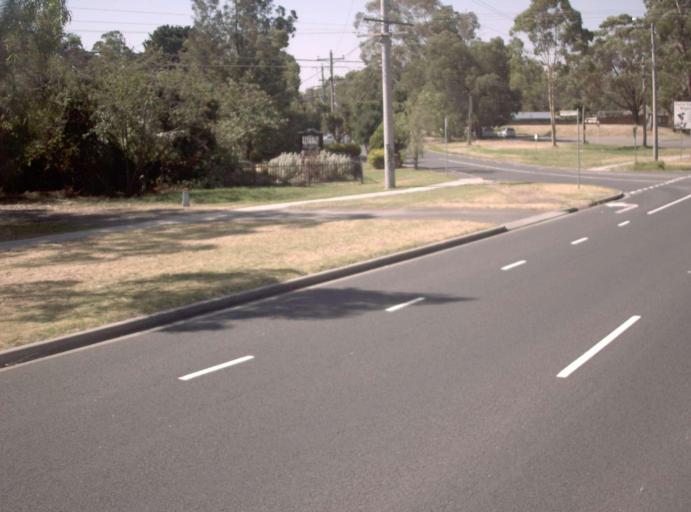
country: AU
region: Victoria
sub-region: Nillumbik
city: Eltham
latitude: -37.7324
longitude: 145.1403
